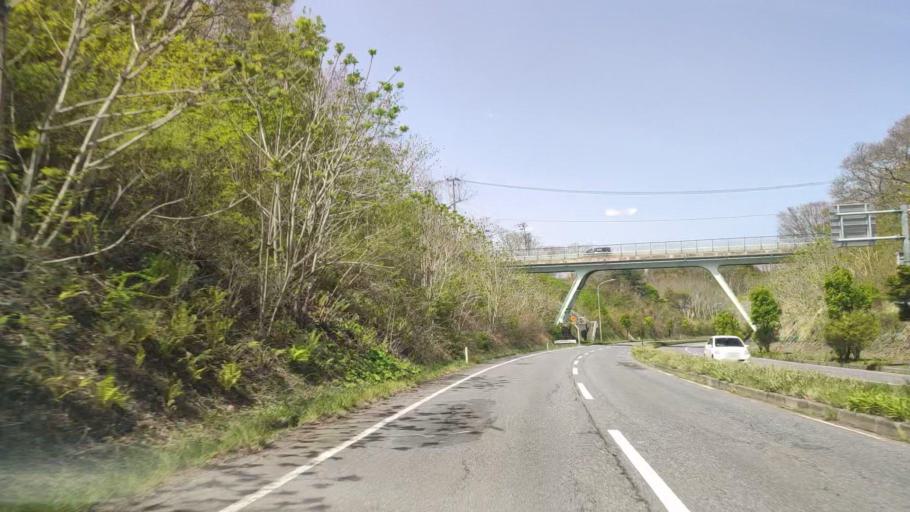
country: JP
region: Aomori
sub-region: Hachinohe Shi
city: Uchimaru
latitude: 40.4961
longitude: 141.4597
